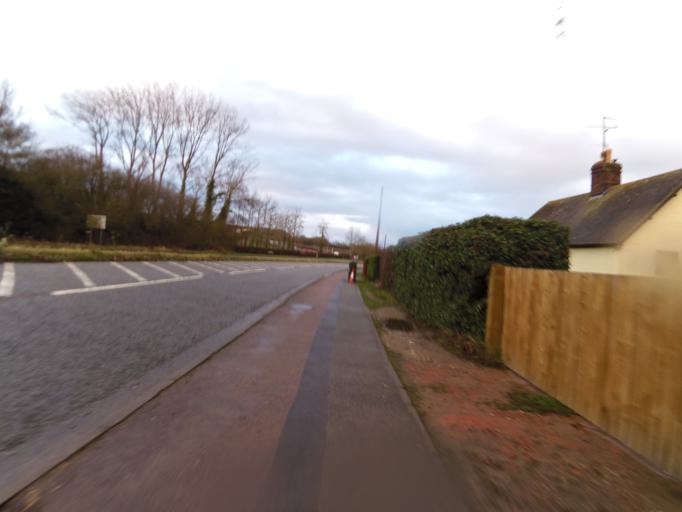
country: GB
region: England
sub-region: Suffolk
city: Stowmarket
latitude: 52.1723
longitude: 1.0178
